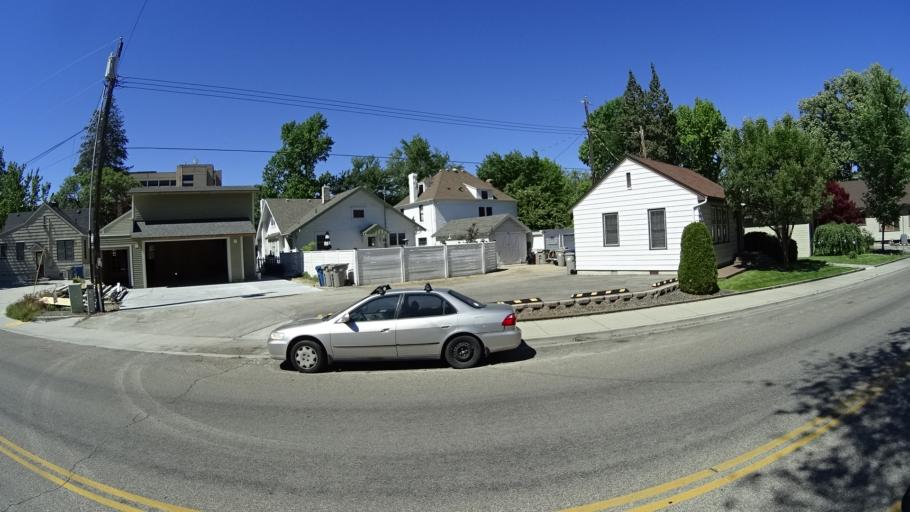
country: US
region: Idaho
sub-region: Ada County
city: Boise
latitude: 43.6186
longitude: -116.1944
